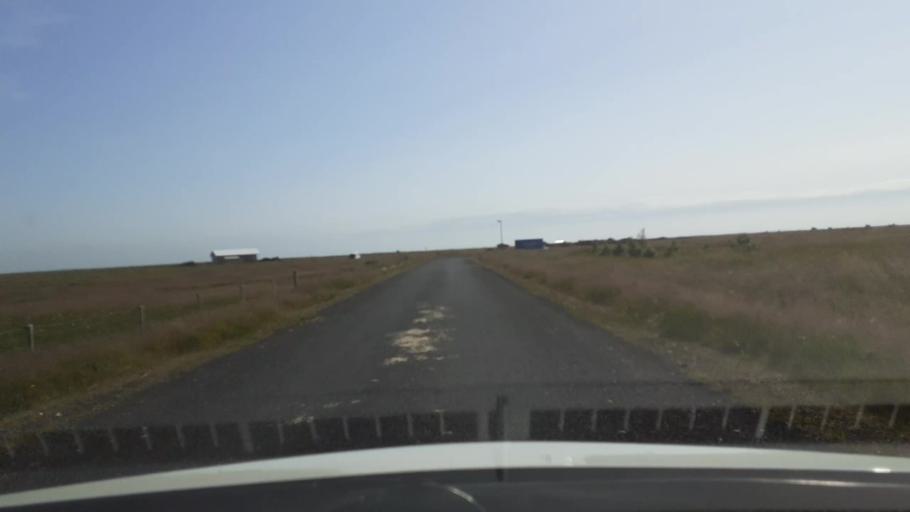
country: IS
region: South
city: Selfoss
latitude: 63.8911
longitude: -21.0862
